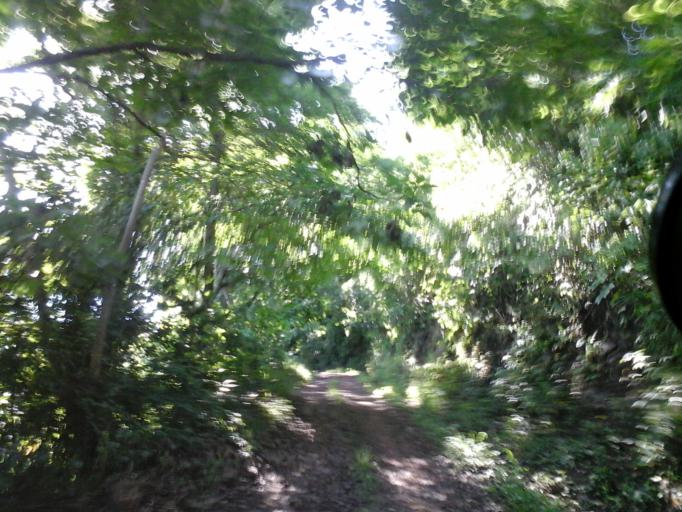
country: CO
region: Cesar
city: San Diego
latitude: 10.2714
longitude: -73.0858
